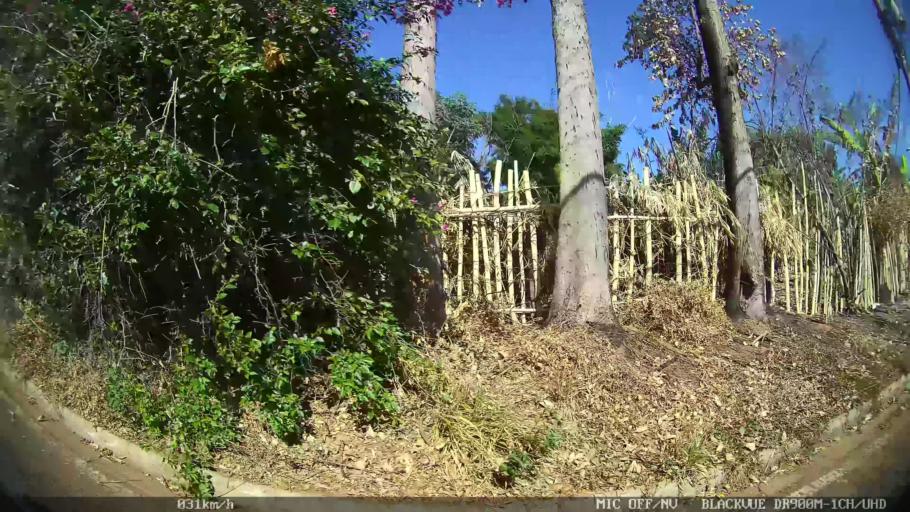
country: BR
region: Sao Paulo
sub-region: Franca
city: Franca
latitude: -20.5387
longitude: -47.4619
